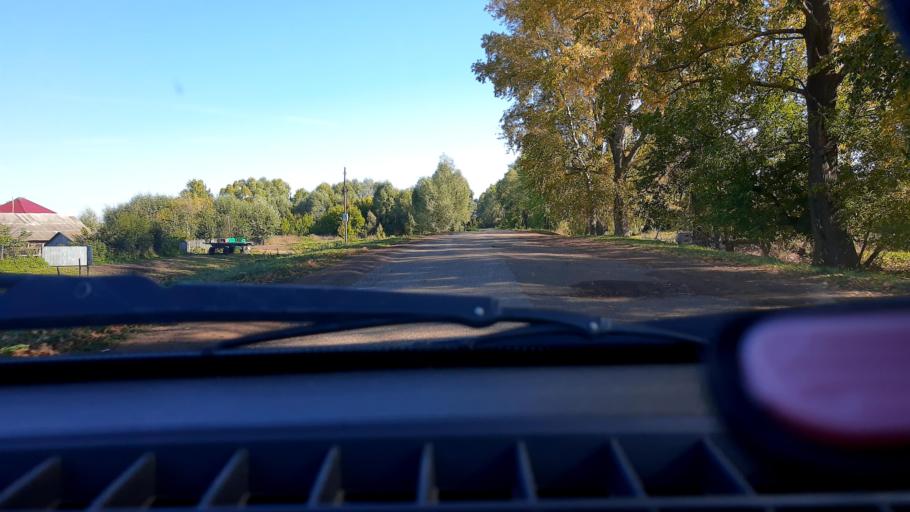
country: RU
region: Bashkortostan
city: Kushnarenkovo
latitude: 55.0994
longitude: 55.5084
